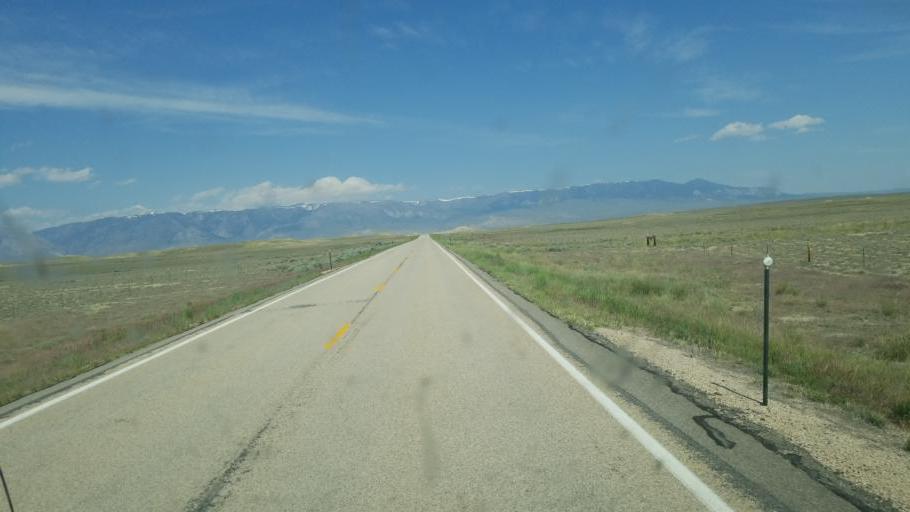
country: US
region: Wyoming
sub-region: Park County
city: Powell
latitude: 44.8679
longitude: -109.0410
